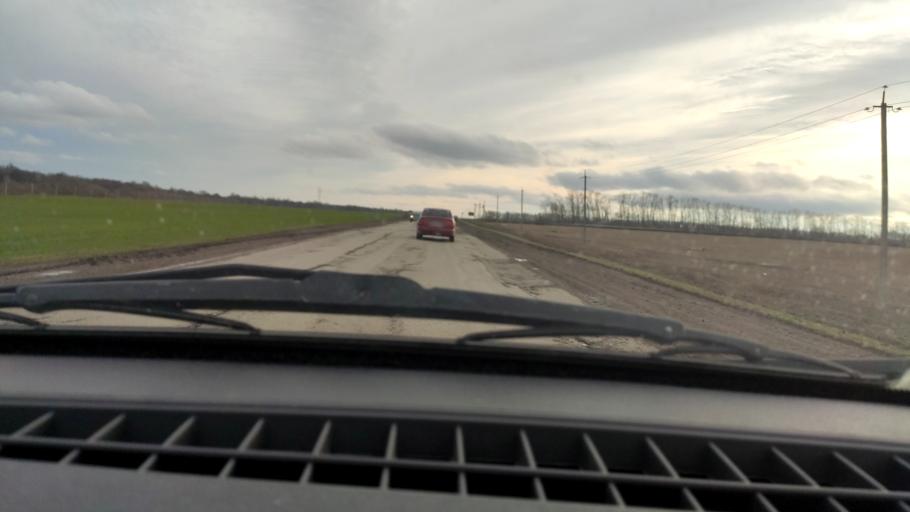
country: RU
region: Bashkortostan
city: Chishmy
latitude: 54.5657
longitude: 55.3486
